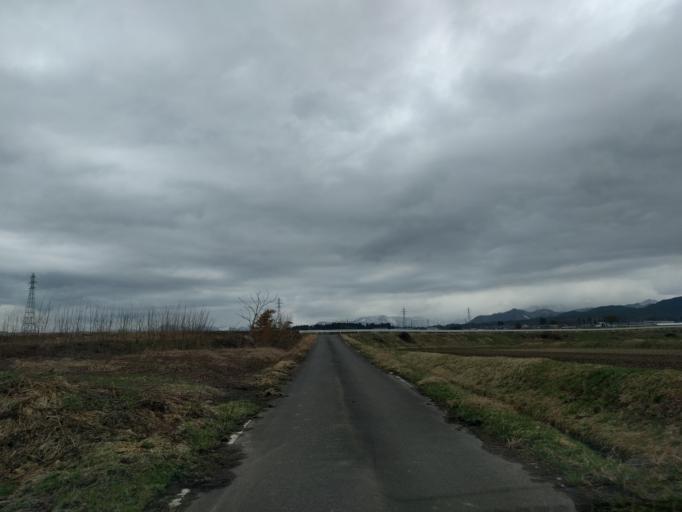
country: JP
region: Fukushima
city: Kitakata
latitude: 37.6507
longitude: 139.9146
